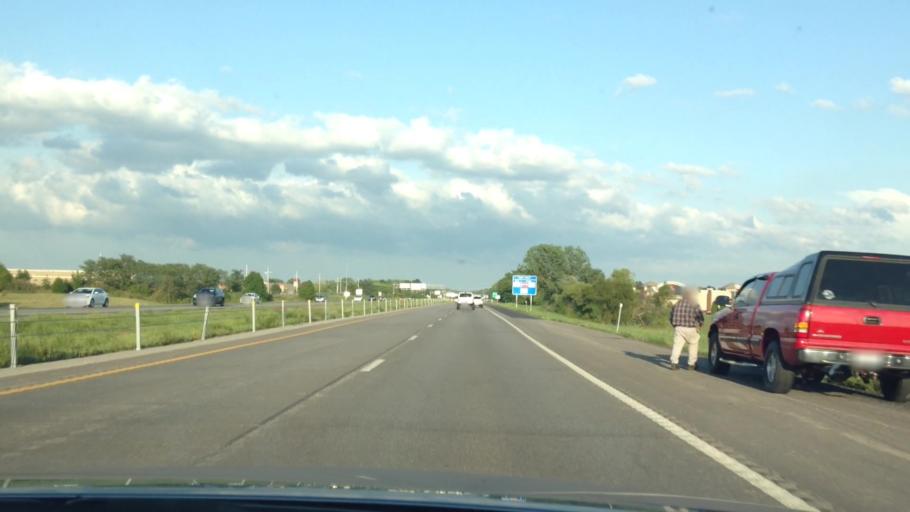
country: US
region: Missouri
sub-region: Platte County
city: Weatherby Lake
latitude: 39.2544
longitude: -94.6561
